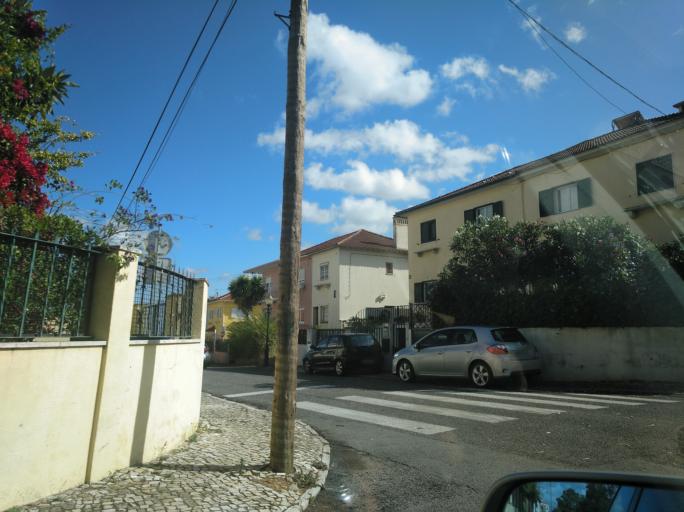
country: PT
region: Lisbon
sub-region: Loures
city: Moscavide
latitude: 38.7750
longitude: -9.1224
